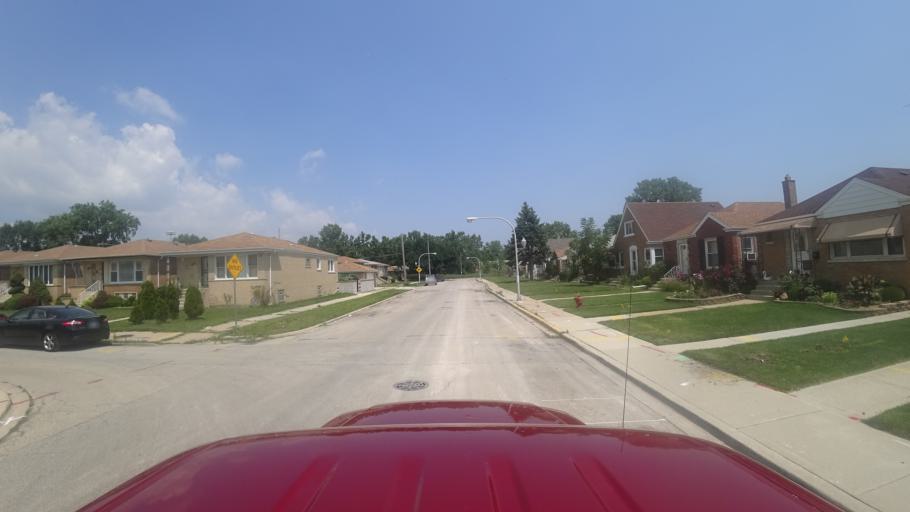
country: US
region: Illinois
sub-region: Cook County
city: Cicero
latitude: 41.8014
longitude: -87.7173
